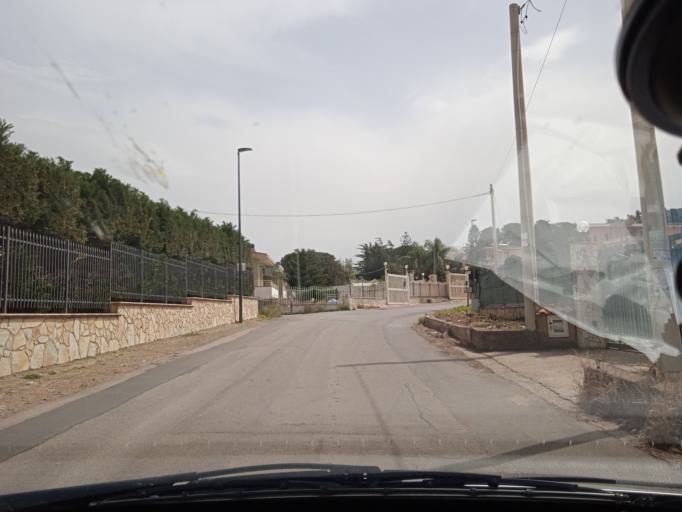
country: IT
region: Sicily
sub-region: Palermo
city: Torre Colonna-Sperone
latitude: 38.0261
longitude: 13.5759
